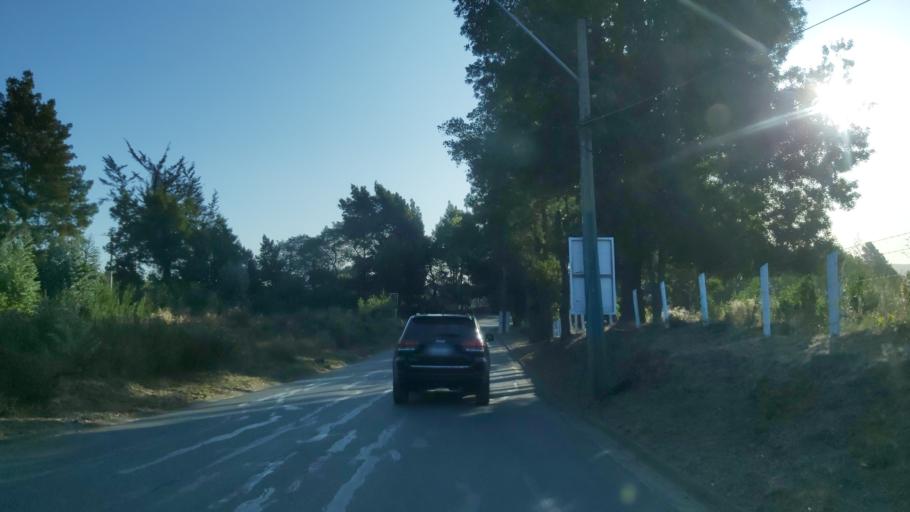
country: CL
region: Biobio
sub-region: Provincia de Concepcion
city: Tome
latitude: -36.5387
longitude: -72.9280
